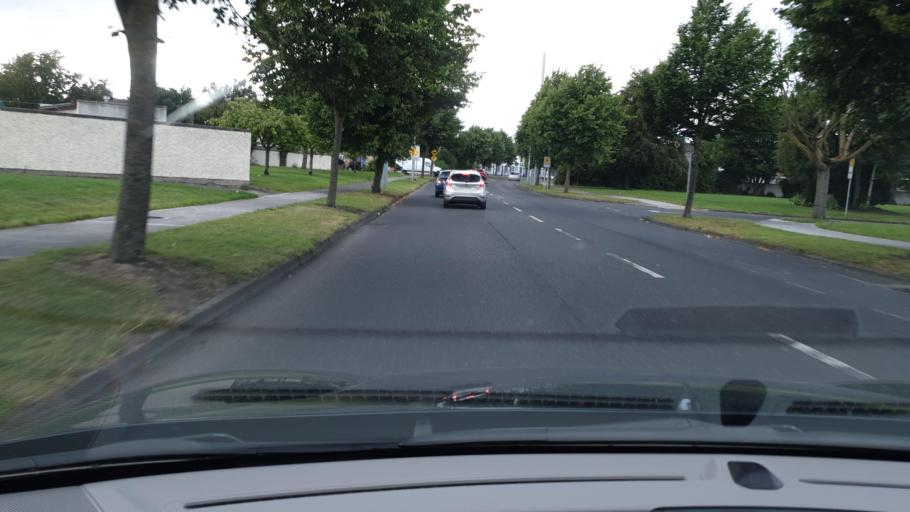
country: IE
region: Leinster
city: Clondalkin
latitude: 53.3233
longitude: -6.4104
